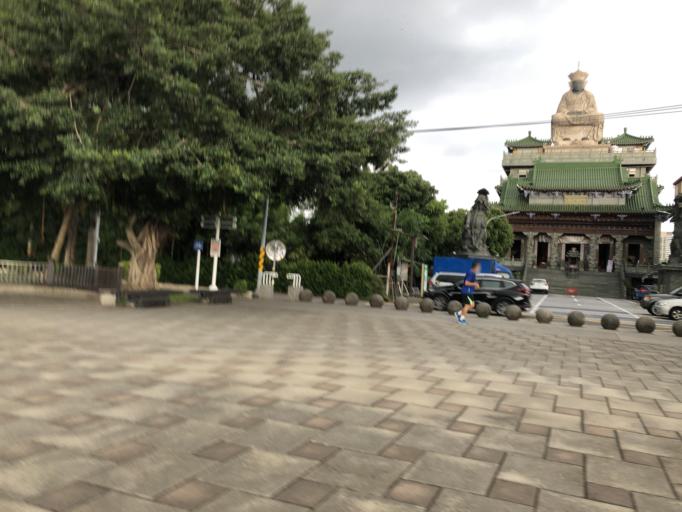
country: TW
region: Kaohsiung
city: Kaohsiung
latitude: 22.6845
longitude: 120.2989
